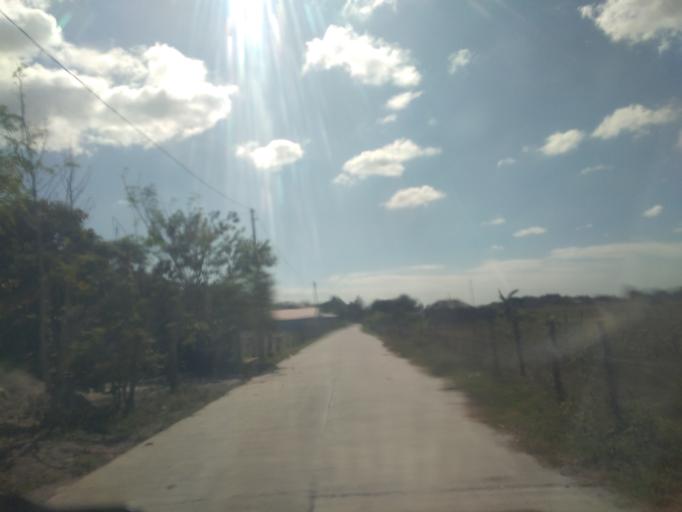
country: PH
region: Central Luzon
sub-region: Province of Pampanga
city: Balas
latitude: 15.0776
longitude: 120.6017
